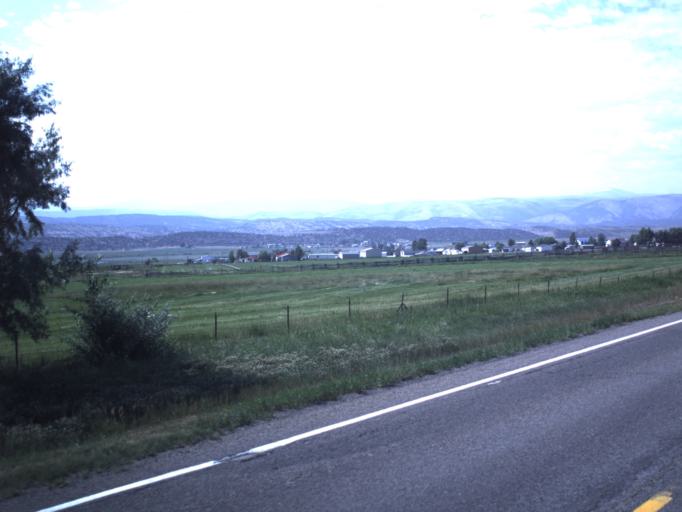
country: US
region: Utah
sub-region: Daggett County
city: Manila
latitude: 40.9954
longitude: -109.6811
